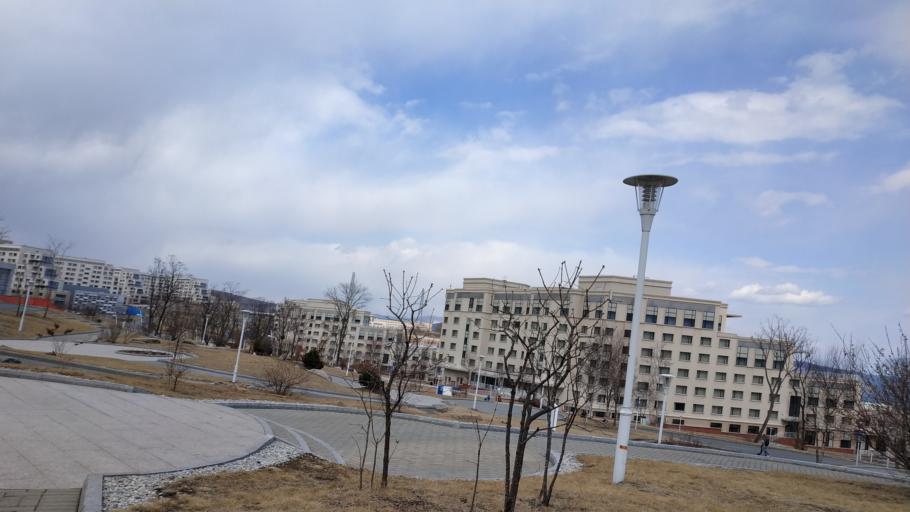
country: RU
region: Primorskiy
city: Russkiy
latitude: 43.0280
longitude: 131.8871
